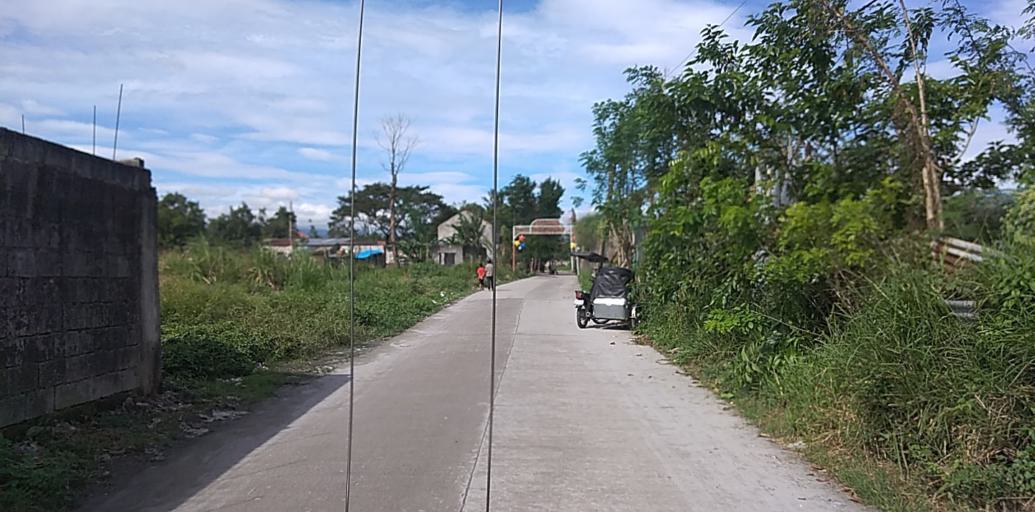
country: PH
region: Central Luzon
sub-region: Province of Pampanga
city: Angeles City
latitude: 15.1300
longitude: 120.5579
